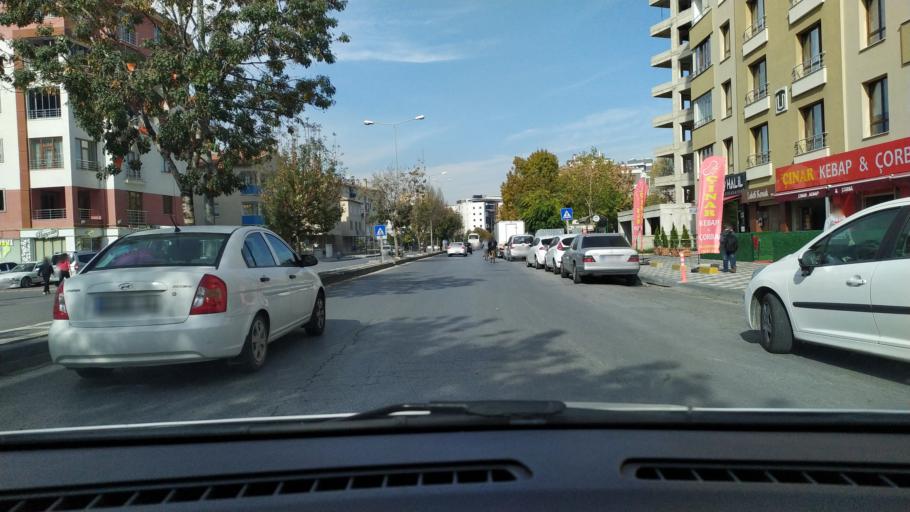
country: TR
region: Kayseri
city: Kayseri
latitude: 38.7090
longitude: 35.4917
